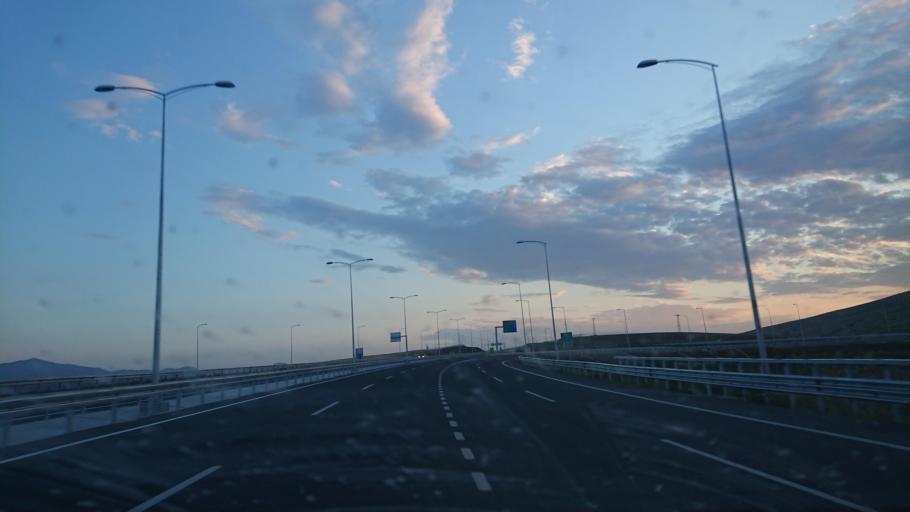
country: TR
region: Aksaray
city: Balci
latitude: 38.7726
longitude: 34.1063
